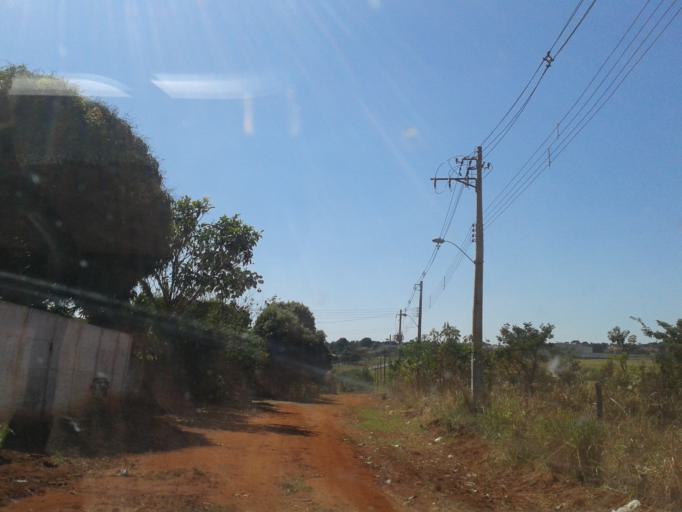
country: BR
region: Minas Gerais
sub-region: Ituiutaba
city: Ituiutaba
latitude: -18.9996
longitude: -49.4729
